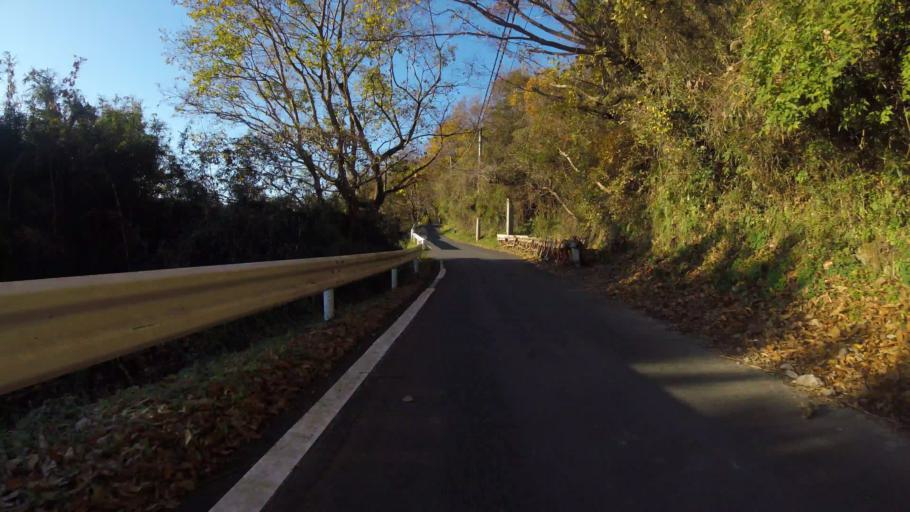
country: JP
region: Shizuoka
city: Mishima
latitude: 35.0037
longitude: 138.9338
